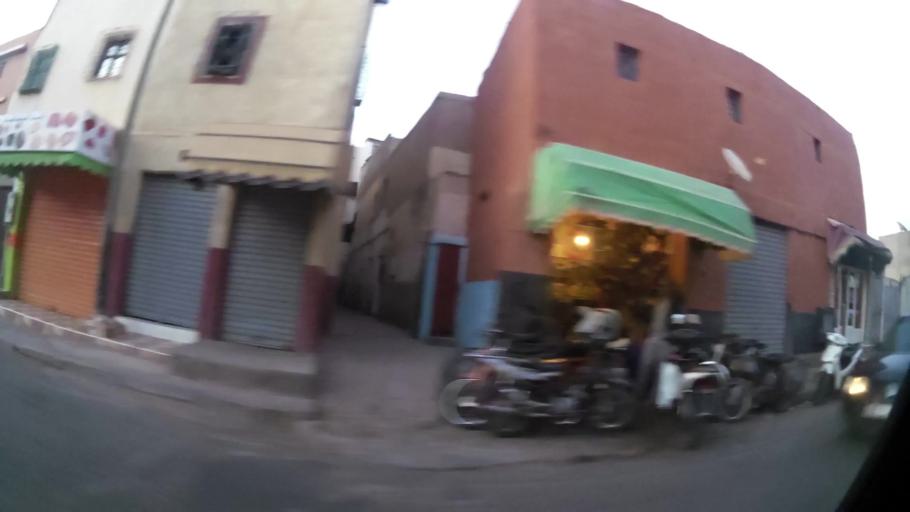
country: MA
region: Souss-Massa-Draa
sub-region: Inezgane-Ait Mellou
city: Inezgane
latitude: 30.3750
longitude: -9.4931
